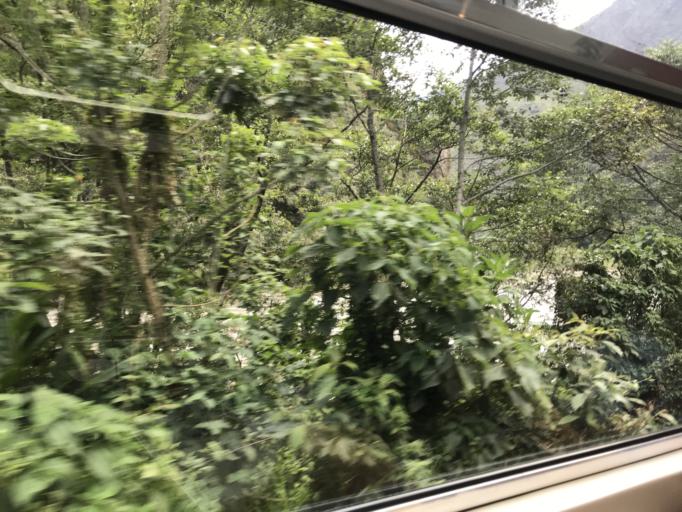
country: PE
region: Cusco
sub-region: Provincia de La Convencion
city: Santa Teresa
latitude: -13.1708
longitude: -72.5019
